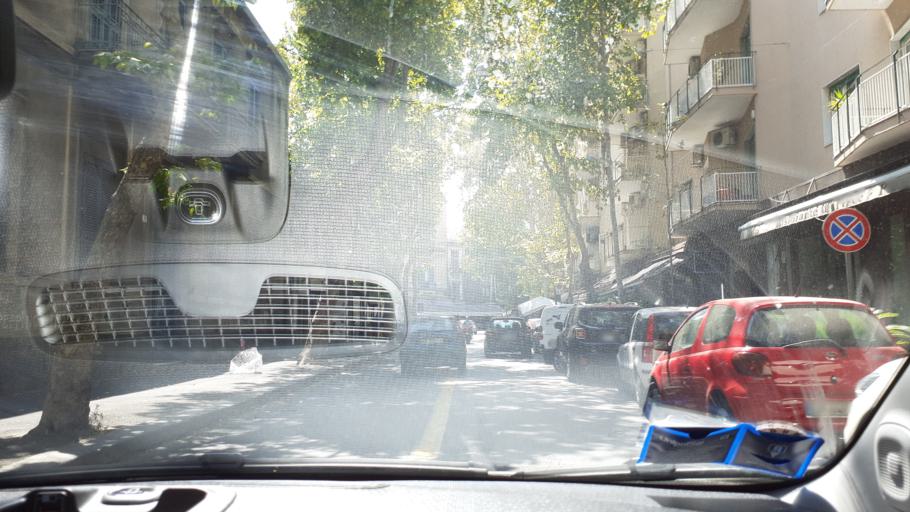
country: IT
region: Sicily
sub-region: Catania
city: Catania
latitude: 37.5081
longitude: 15.0794
